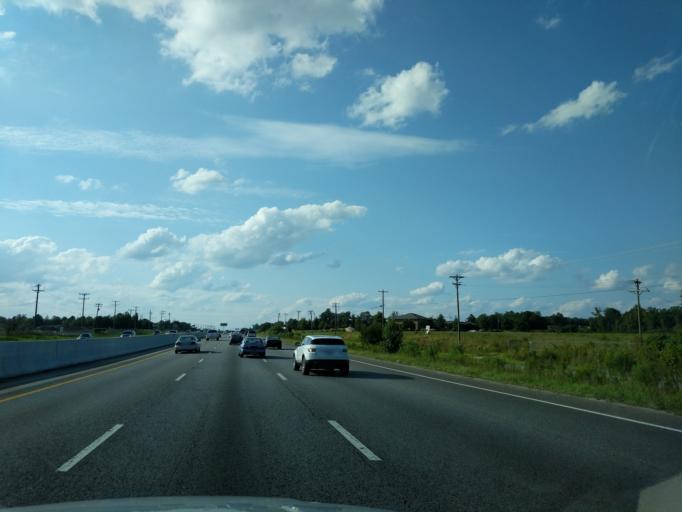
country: US
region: South Carolina
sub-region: Greenville County
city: Simpsonville
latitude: 34.7079
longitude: -82.2429
